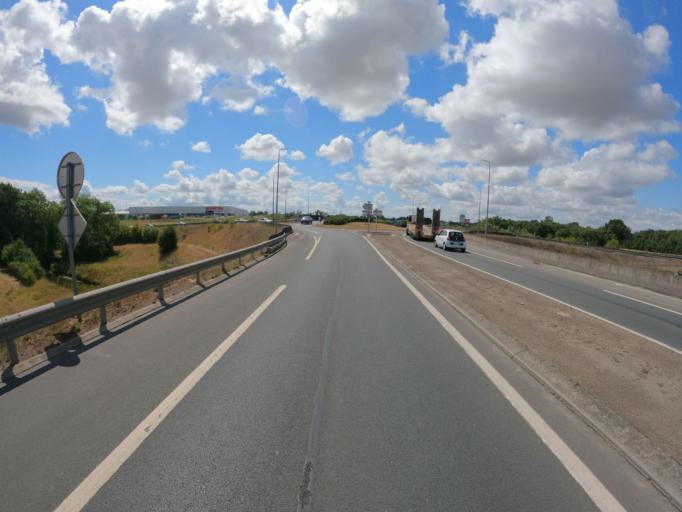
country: FR
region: Pays de la Loire
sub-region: Departement de la Loire-Atlantique
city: Saint-Gereon
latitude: 47.3922
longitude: -1.1887
